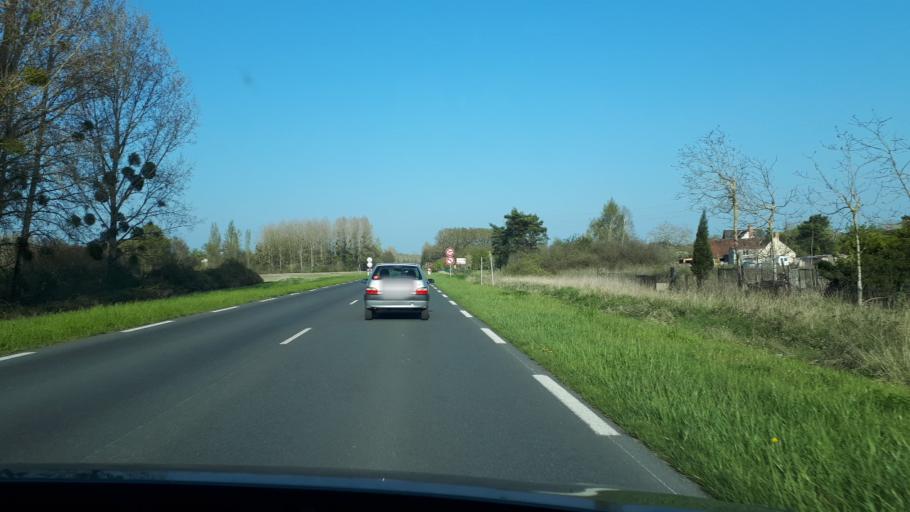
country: FR
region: Centre
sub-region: Departement du Loir-et-Cher
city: Saint-Georges-sur-Cher
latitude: 47.3247
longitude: 1.1054
